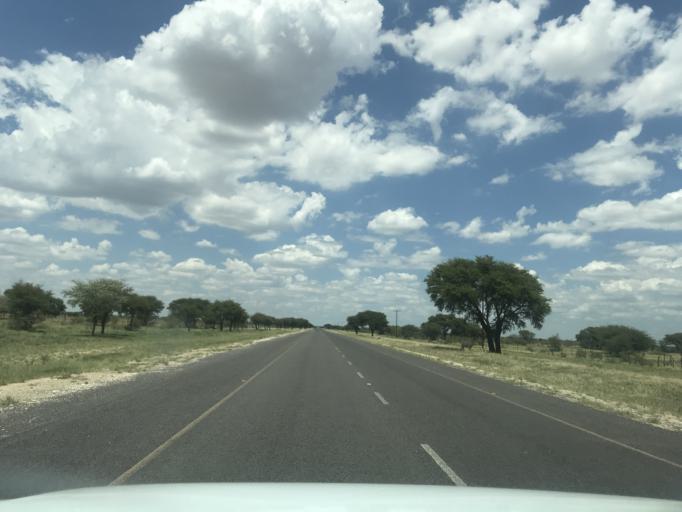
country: BW
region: South East
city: Janeng
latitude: -25.6945
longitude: 25.1277
